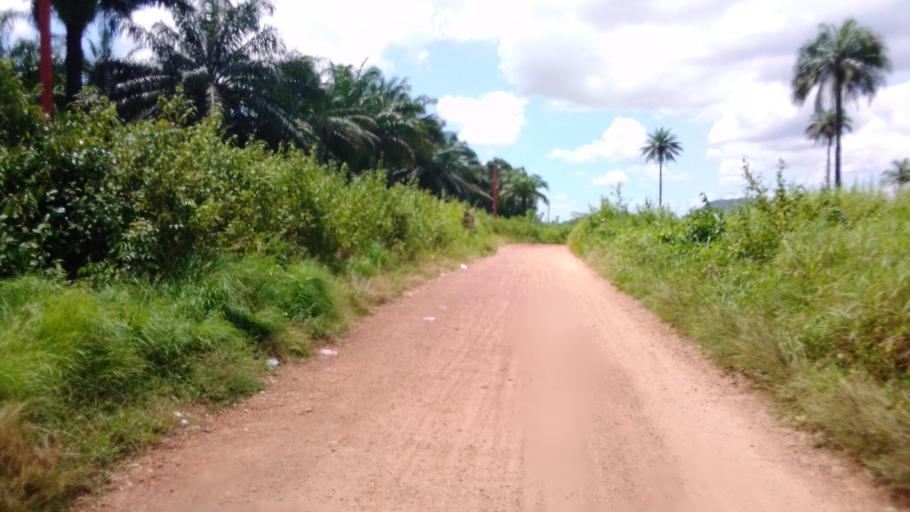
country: SL
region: Northern Province
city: Makeni
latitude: 8.8759
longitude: -12.0119
